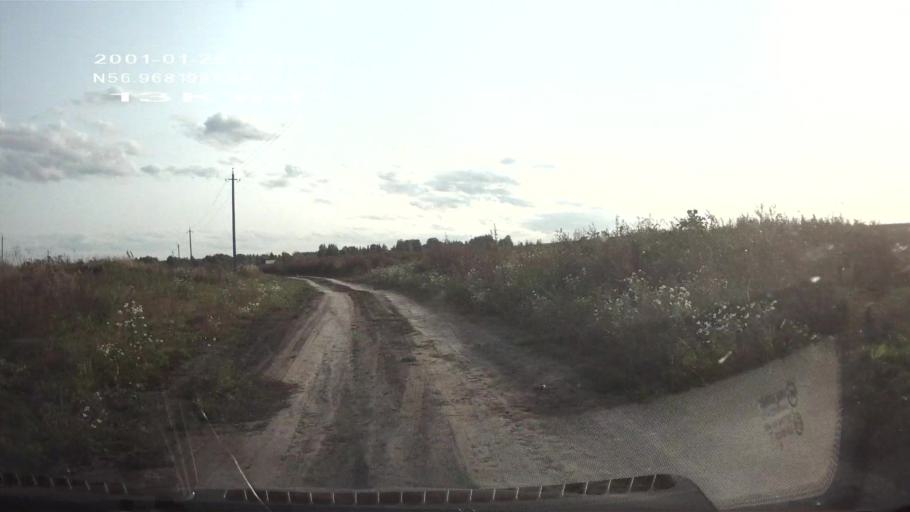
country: RU
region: Mariy-El
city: Kuzhener
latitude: 56.9680
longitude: 48.7841
